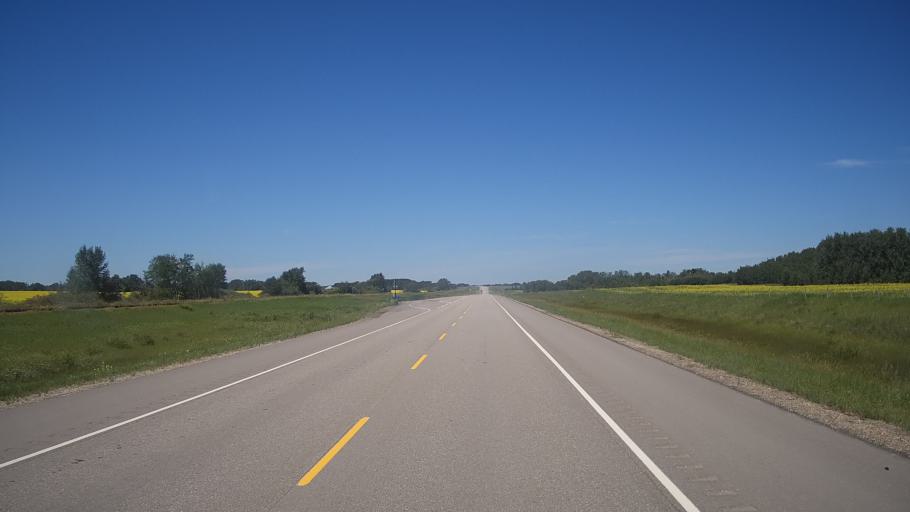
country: CA
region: Manitoba
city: Minnedosa
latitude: 50.2797
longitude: -99.9551
